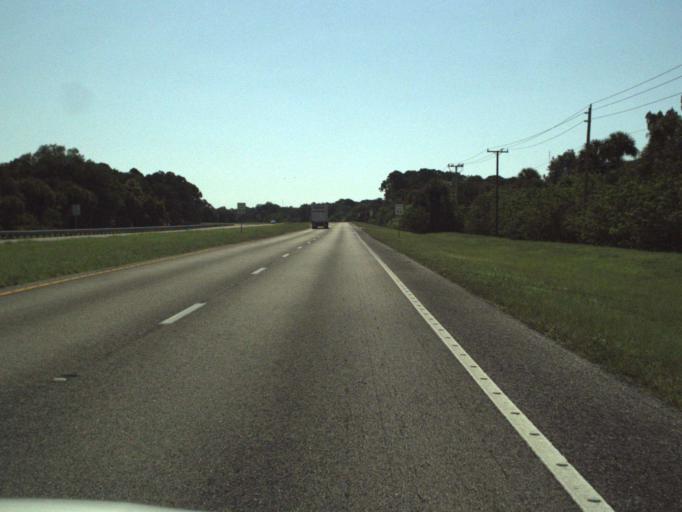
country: US
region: Florida
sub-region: Brevard County
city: Cocoa West
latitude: 28.3610
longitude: -80.8306
